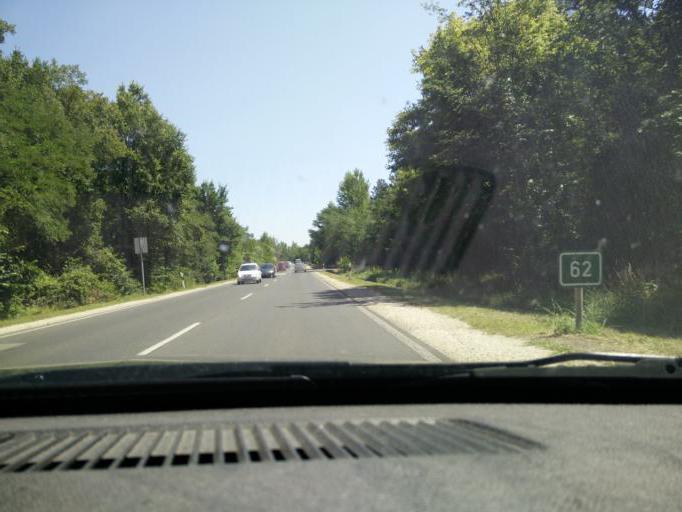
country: HU
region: Komarom-Esztergom
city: Baj
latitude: 47.6335
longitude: 18.3543
